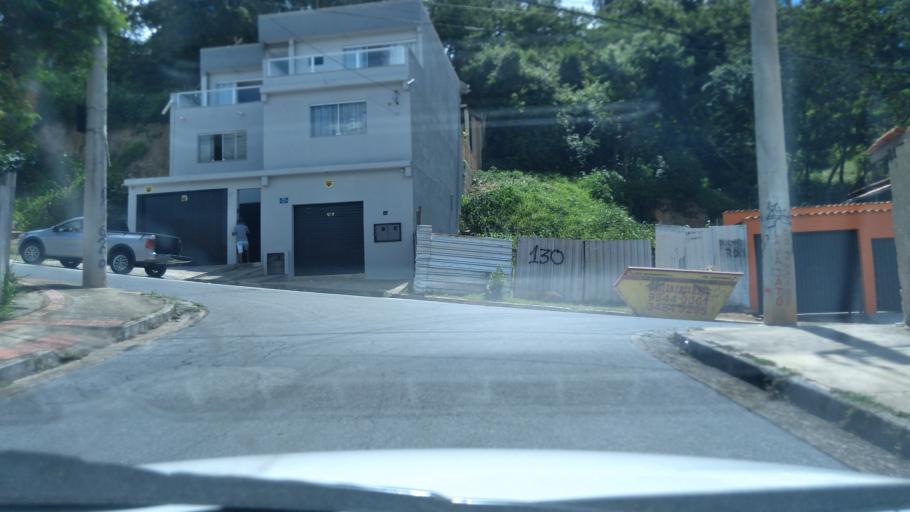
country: BR
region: Minas Gerais
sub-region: Belo Horizonte
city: Belo Horizonte
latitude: -19.8576
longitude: -43.8794
